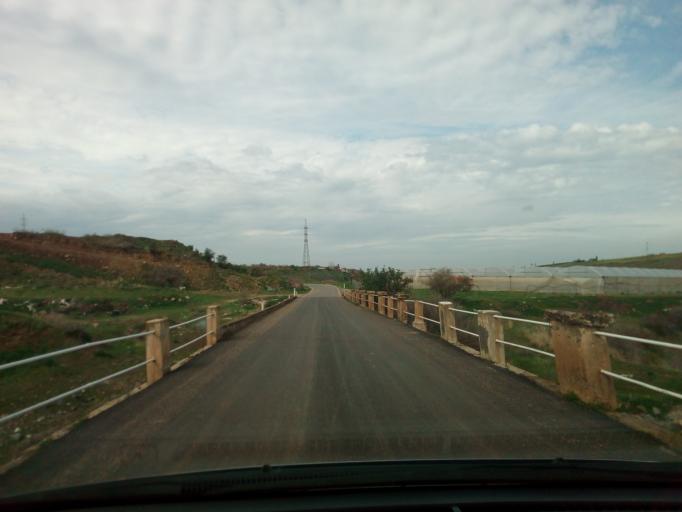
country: CY
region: Lefkosia
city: Astromeritis
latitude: 35.0950
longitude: 32.9905
